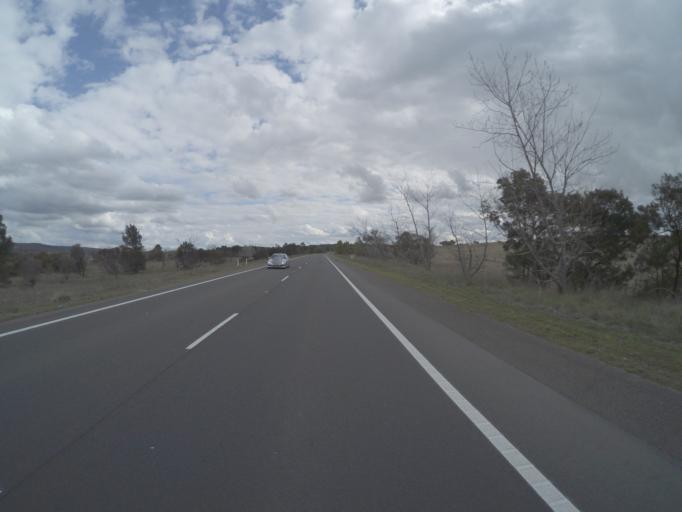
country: AU
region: New South Wales
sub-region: Goulburn Mulwaree
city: Goulburn
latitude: -34.8023
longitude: 149.6090
